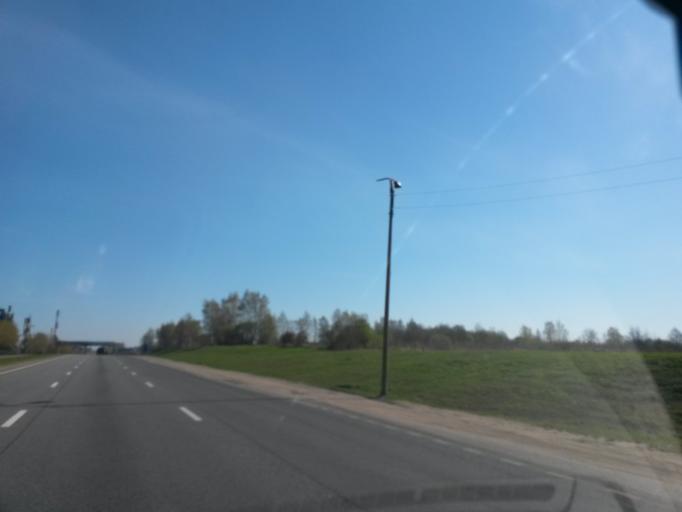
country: RU
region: Jaroslavl
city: Krasnyye Tkachi
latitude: 57.5360
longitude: 39.7897
